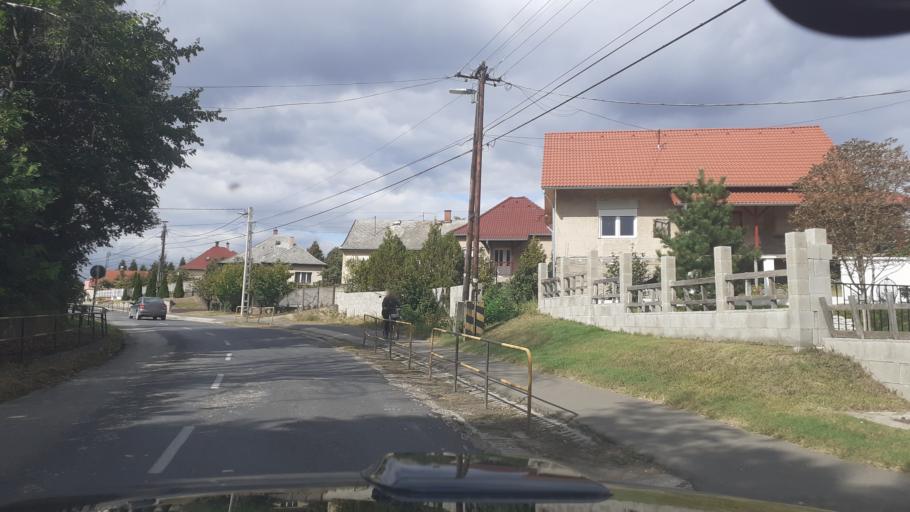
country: HU
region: Bacs-Kiskun
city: Solt
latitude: 46.8105
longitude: 18.9870
